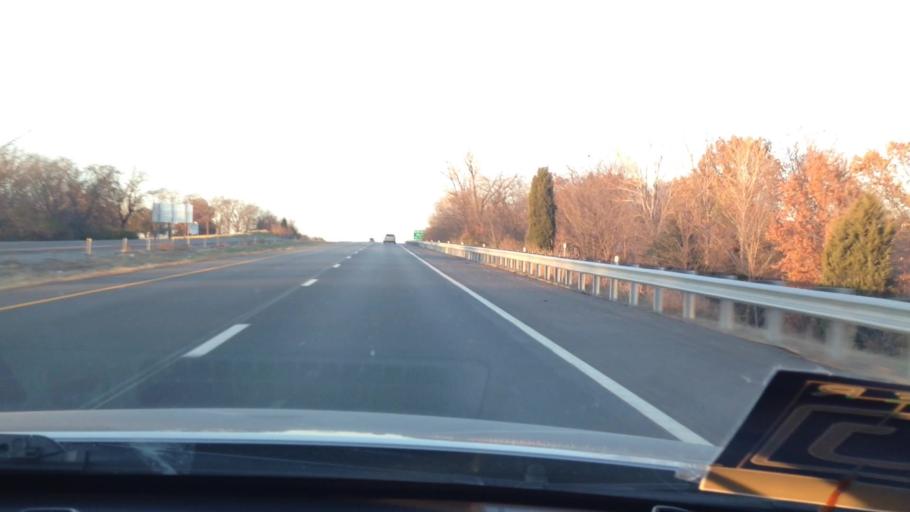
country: US
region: Missouri
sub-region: Platte County
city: Riverside
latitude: 39.2035
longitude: -94.5897
